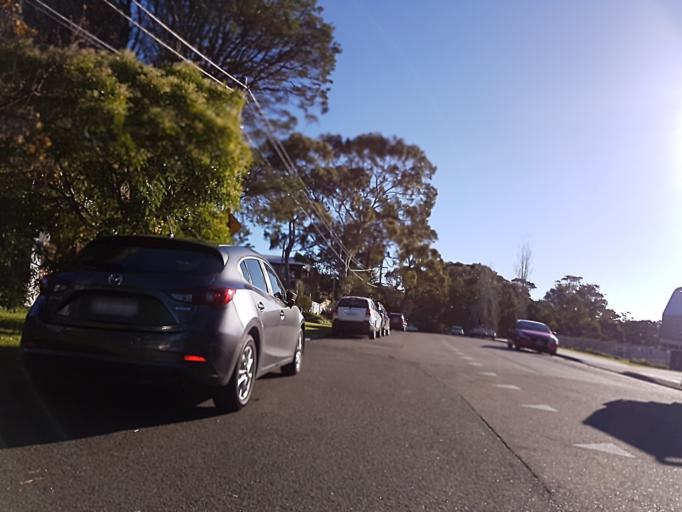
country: AU
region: New South Wales
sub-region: Manly Vale
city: Balgowlah
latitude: -33.7840
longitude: 151.2451
